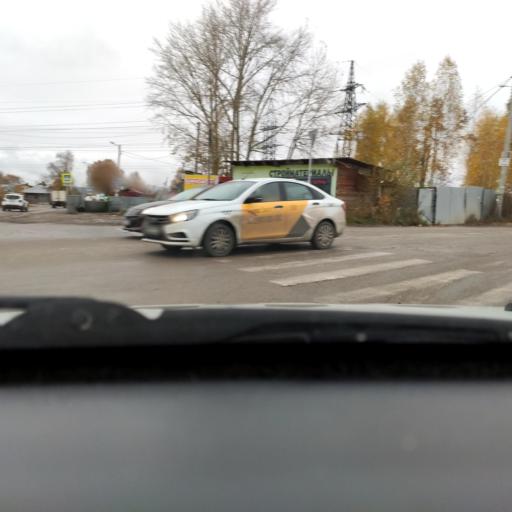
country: RU
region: Perm
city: Perm
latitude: 58.0116
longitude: 56.3199
